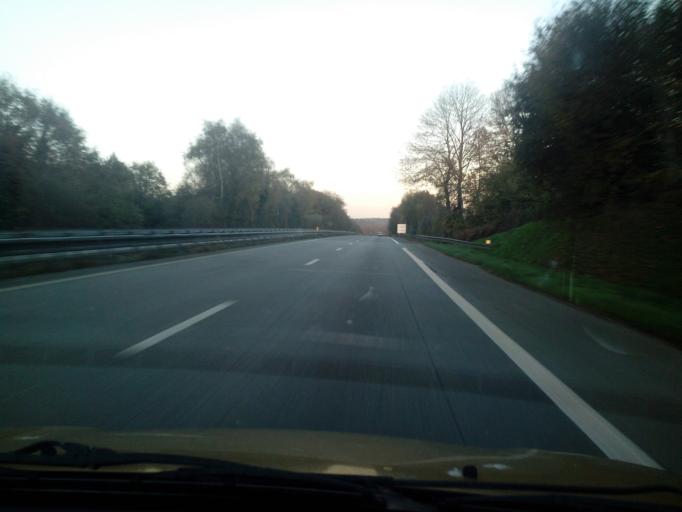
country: FR
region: Brittany
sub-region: Departement du Morbihan
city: Baud
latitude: 47.8644
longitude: -3.0766
